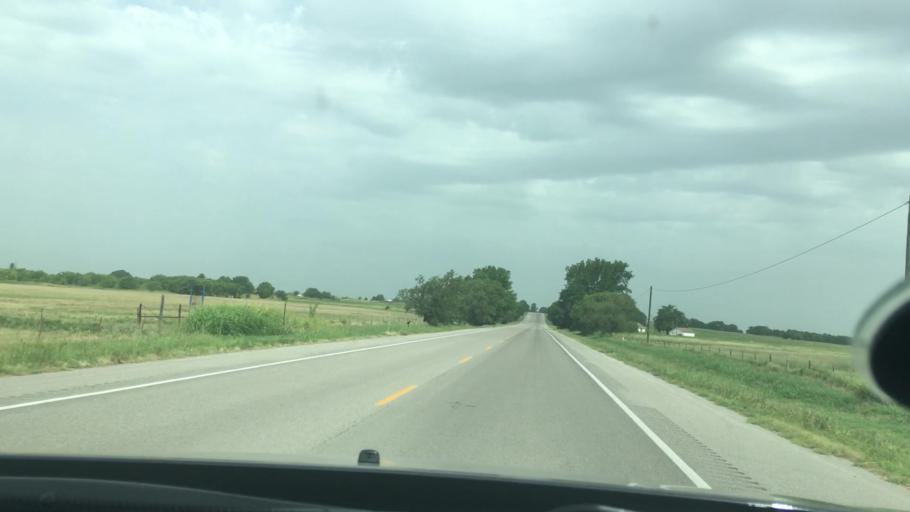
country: US
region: Oklahoma
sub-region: Garvin County
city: Pauls Valley
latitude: 34.8380
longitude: -97.2690
